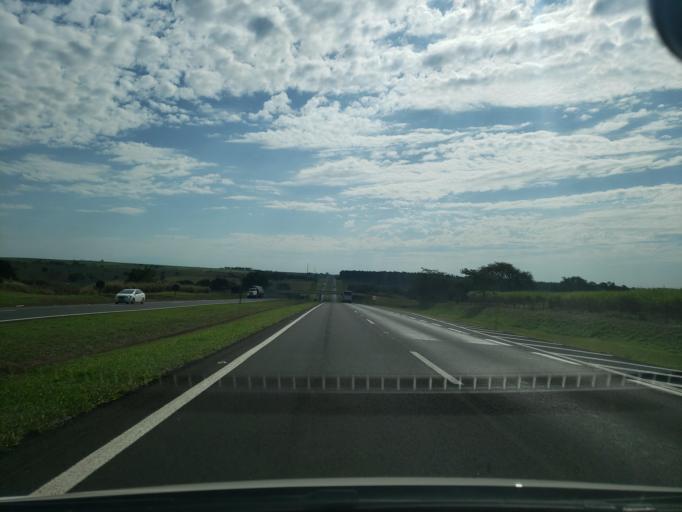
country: BR
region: Sao Paulo
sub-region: Promissao
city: Promissao
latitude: -21.6142
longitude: -49.8642
